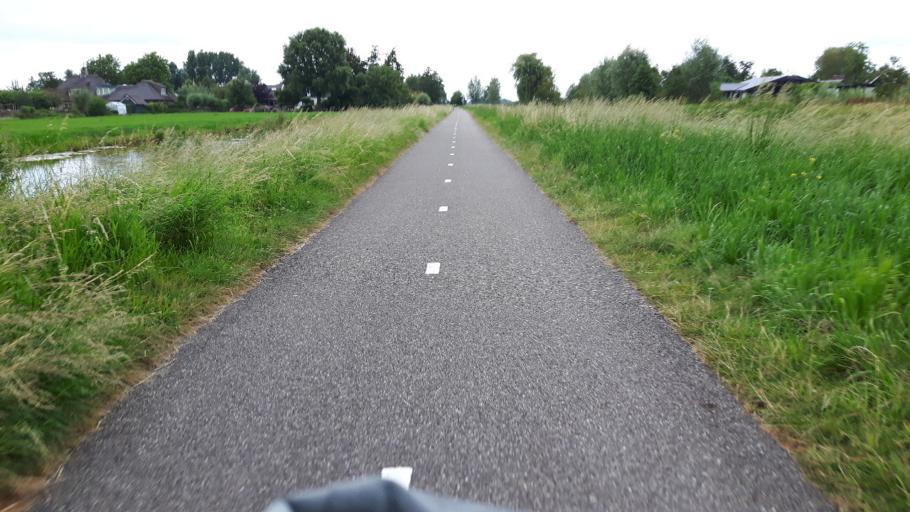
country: NL
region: South Holland
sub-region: Molenwaard
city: Nieuw-Lekkerland
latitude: 51.9335
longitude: 4.7374
